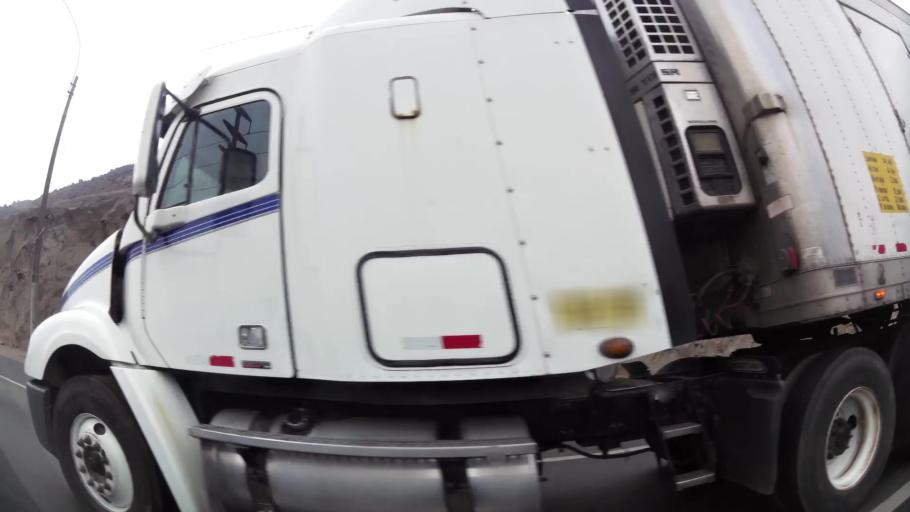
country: PE
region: Lima
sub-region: Lima
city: Vitarte
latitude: -12.0292
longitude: -76.9781
